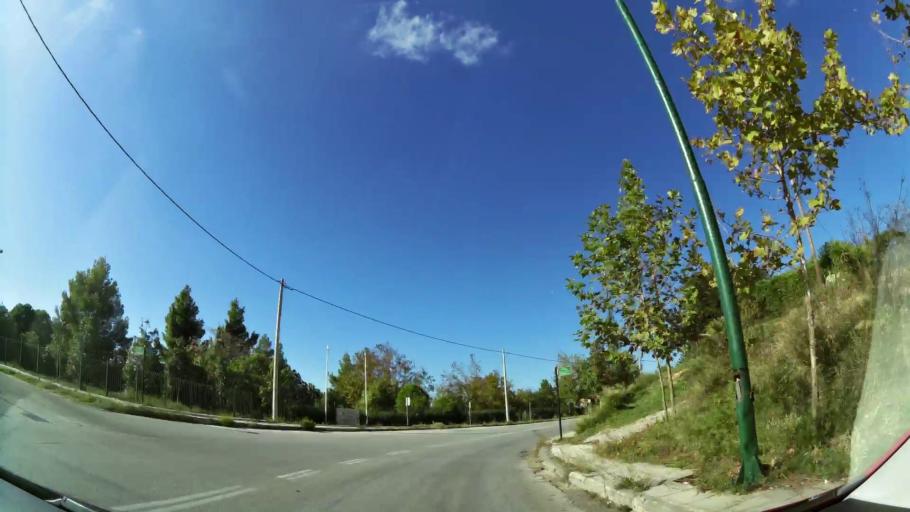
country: GR
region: Attica
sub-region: Nomarchia Anatolikis Attikis
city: Anthousa
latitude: 38.0209
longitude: 23.8713
